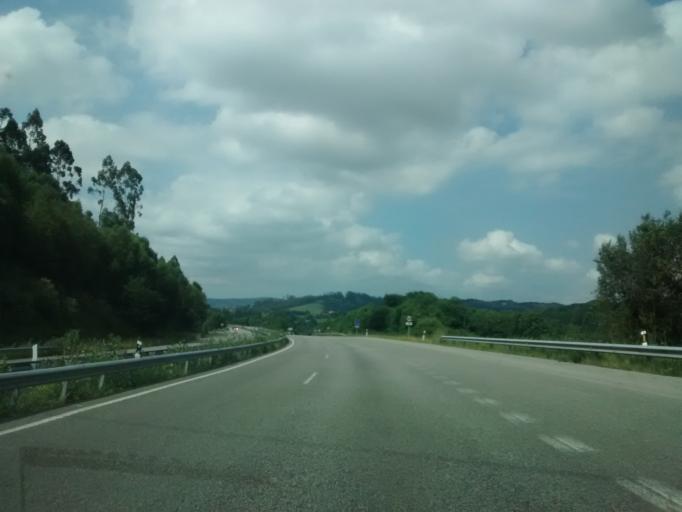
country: ES
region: Asturias
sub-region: Province of Asturias
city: Pola de Siero
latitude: 43.3510
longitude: -5.6810
